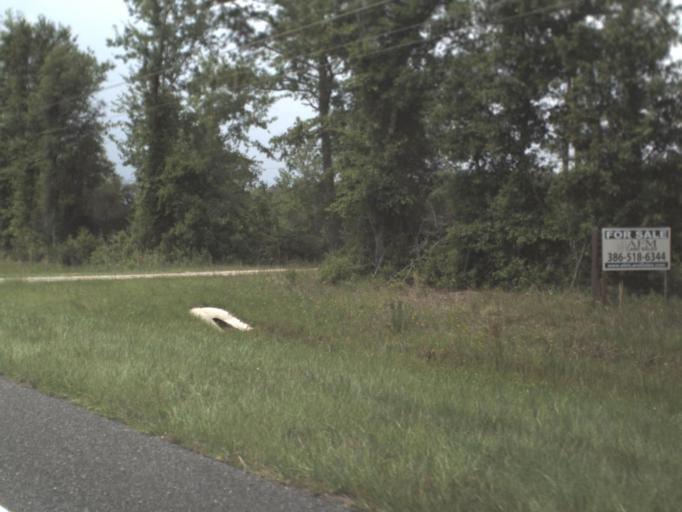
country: US
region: Florida
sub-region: Levy County
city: Chiefland
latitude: 29.3436
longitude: -82.7785
